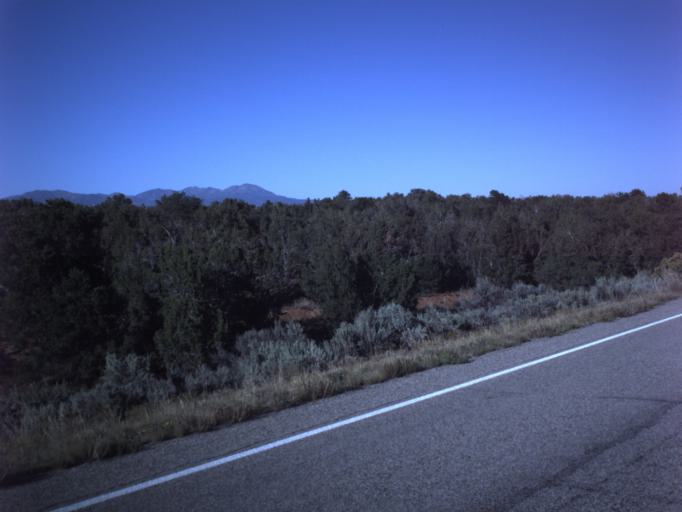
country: US
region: Utah
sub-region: San Juan County
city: Blanding
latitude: 37.5335
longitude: -109.7145
